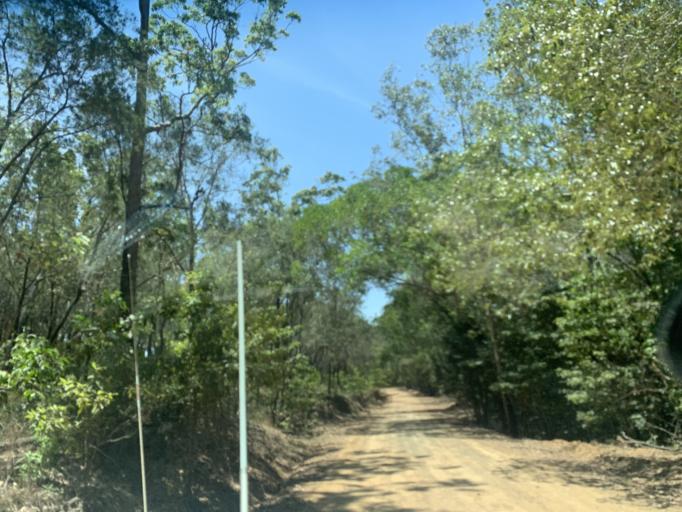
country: AU
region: Queensland
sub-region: Cairns
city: Redlynch
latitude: -16.9254
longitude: 145.6035
